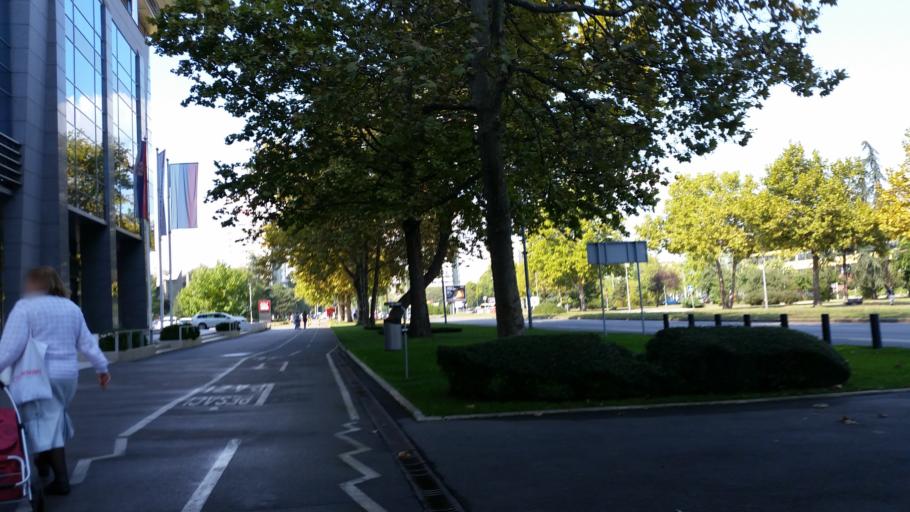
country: RS
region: Central Serbia
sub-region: Belgrade
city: Novi Beograd
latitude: 44.8227
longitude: 20.4162
